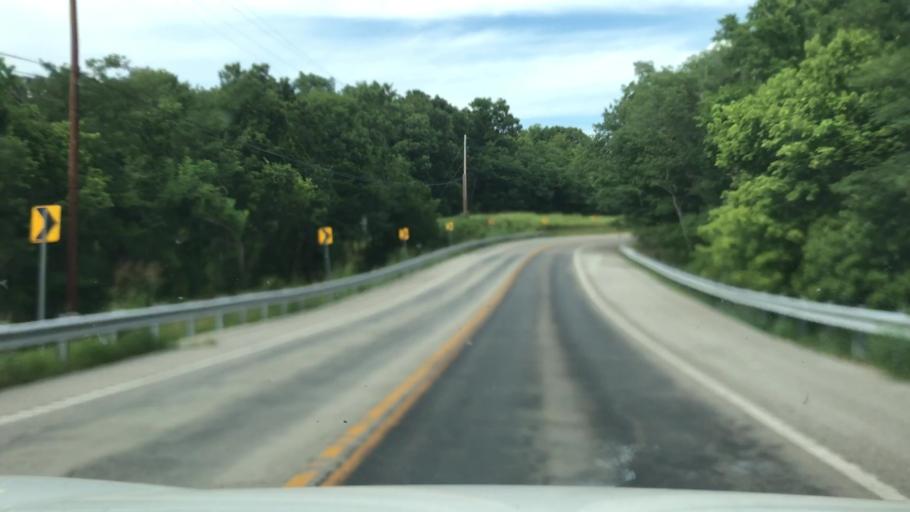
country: US
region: Missouri
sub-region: Saint Charles County
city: Weldon Spring
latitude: 38.6903
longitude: -90.7279
